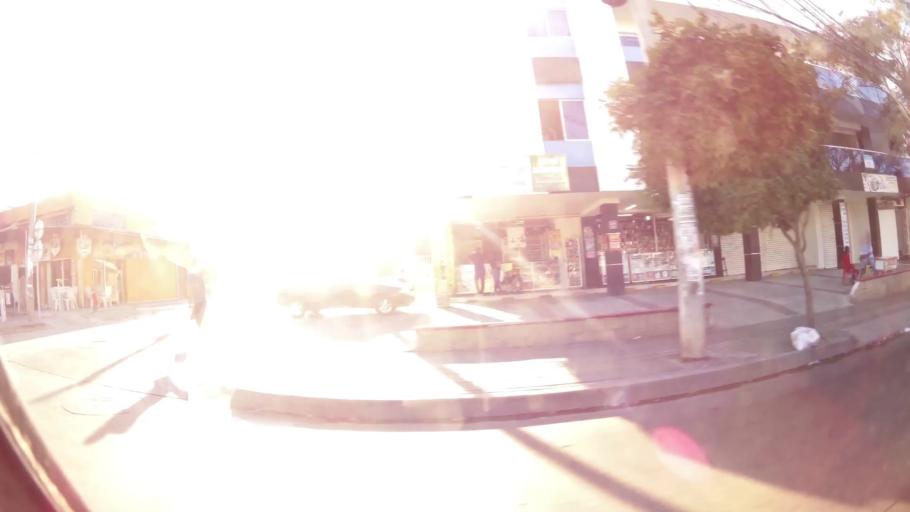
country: CO
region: Atlantico
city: Barranquilla
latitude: 10.9456
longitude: -74.7998
